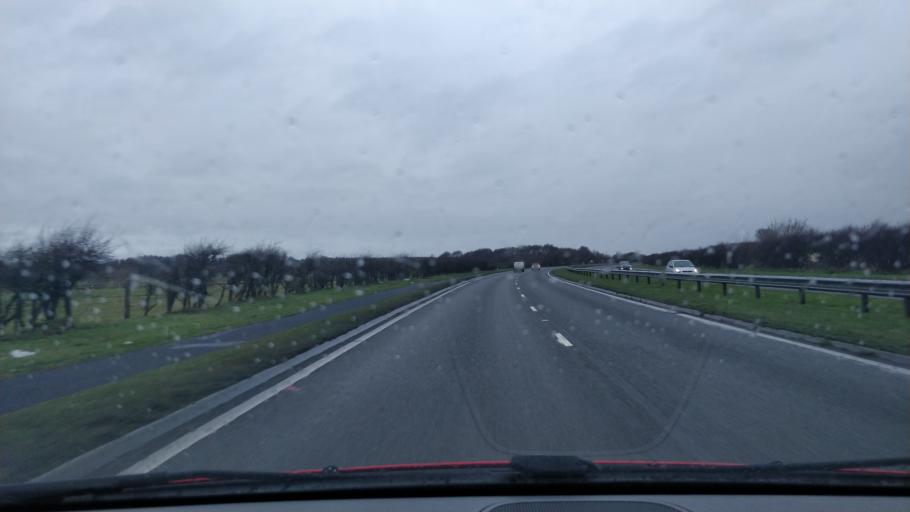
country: GB
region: England
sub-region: Sefton
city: Formby
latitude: 53.5734
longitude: -3.0510
